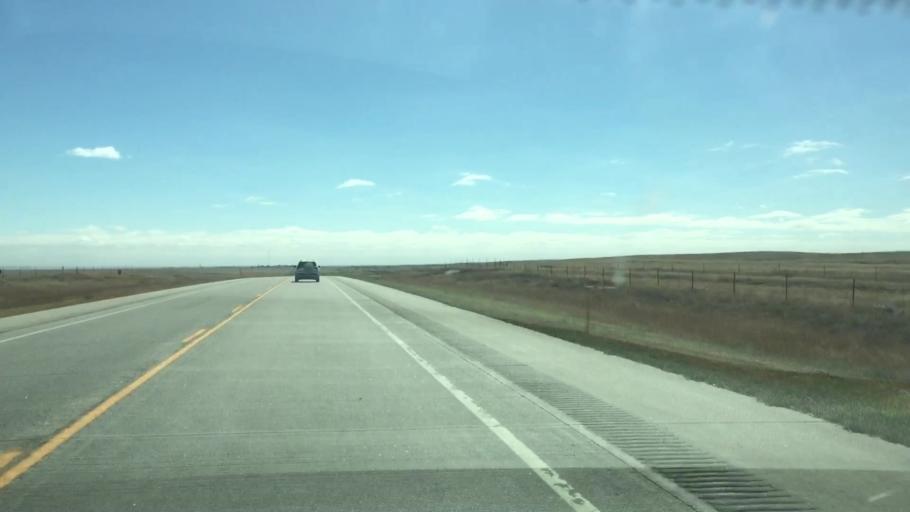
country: US
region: Colorado
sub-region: Lincoln County
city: Hugo
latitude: 39.1760
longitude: -103.5394
